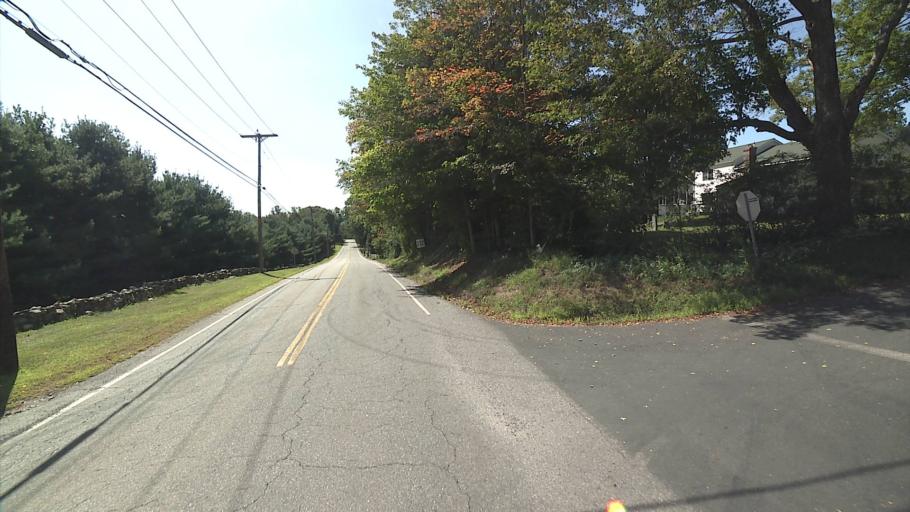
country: US
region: Connecticut
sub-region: Litchfield County
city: Northwest Harwinton
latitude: 41.7537
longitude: -73.0819
